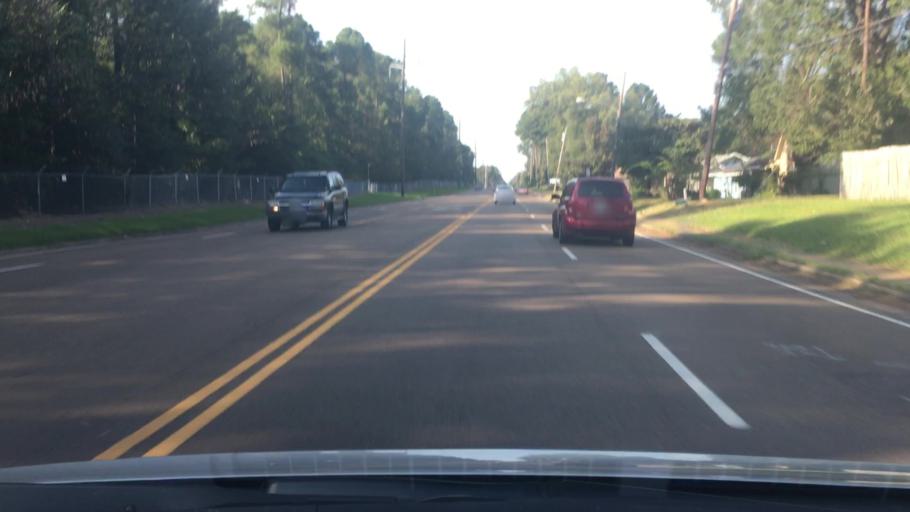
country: US
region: Mississippi
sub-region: Hinds County
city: Jackson
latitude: 32.3639
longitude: -90.1927
